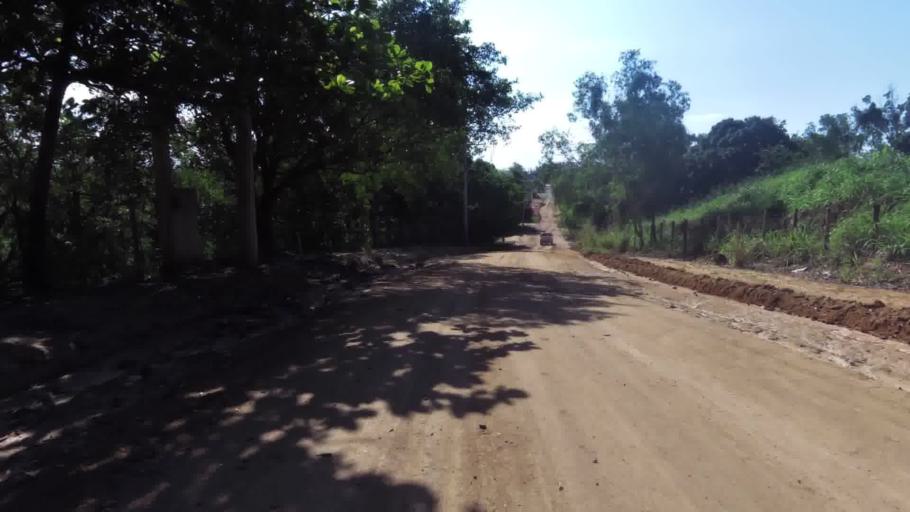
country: BR
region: Espirito Santo
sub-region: Piuma
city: Piuma
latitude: -20.8235
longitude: -40.6256
